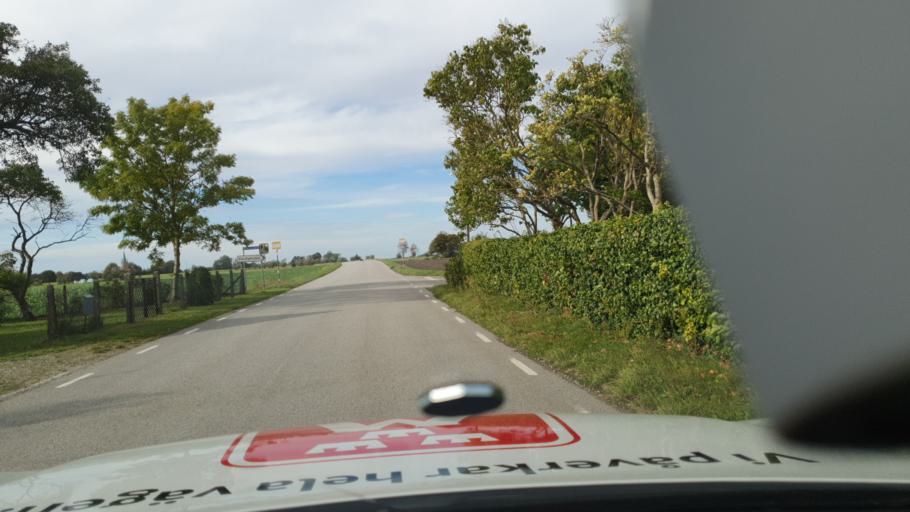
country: SE
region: Skane
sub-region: Vellinge Kommun
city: Vellinge
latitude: 55.5039
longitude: 13.0494
